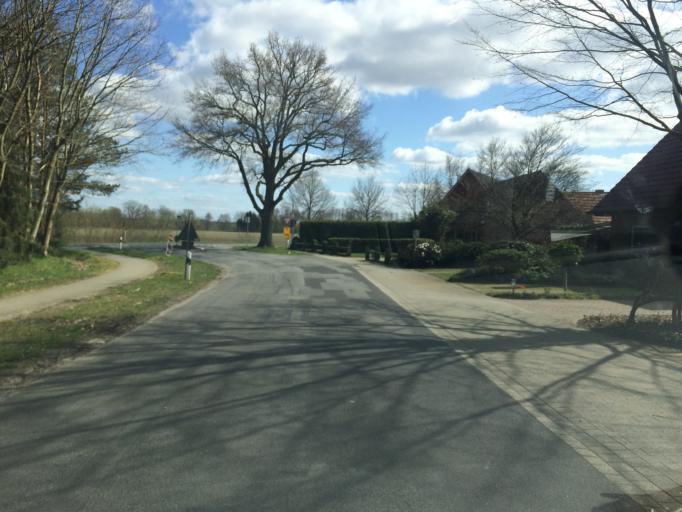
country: DE
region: Lower Saxony
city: Haren
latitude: 52.7642
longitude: 7.2135
